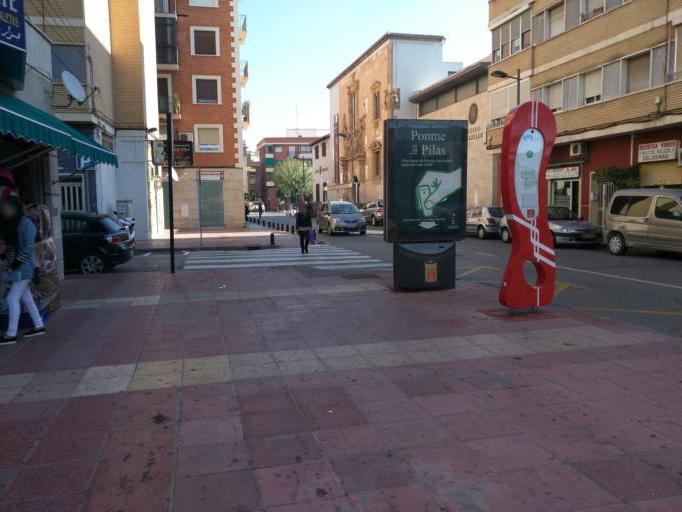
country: ES
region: Murcia
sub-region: Murcia
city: Murcia
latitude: 37.9869
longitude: -1.1391
